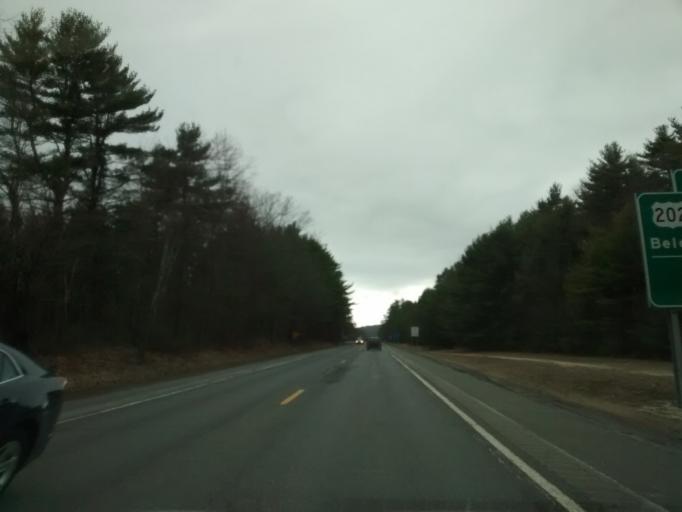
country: US
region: Massachusetts
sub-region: Franklin County
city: Orange
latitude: 42.5619
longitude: -72.2766
